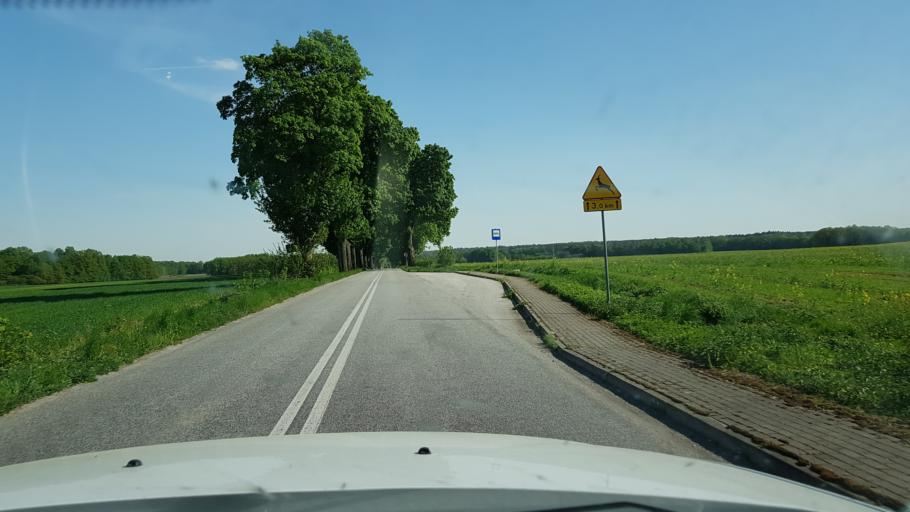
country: PL
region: West Pomeranian Voivodeship
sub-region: Powiat lobeski
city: Resko
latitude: 53.8294
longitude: 15.3889
